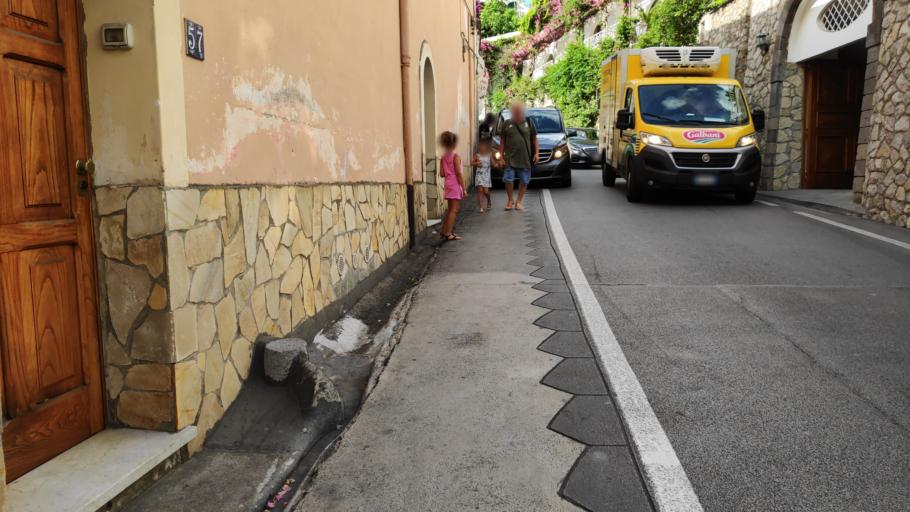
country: IT
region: Campania
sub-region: Provincia di Salerno
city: Positano
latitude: 40.6292
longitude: 14.4852
